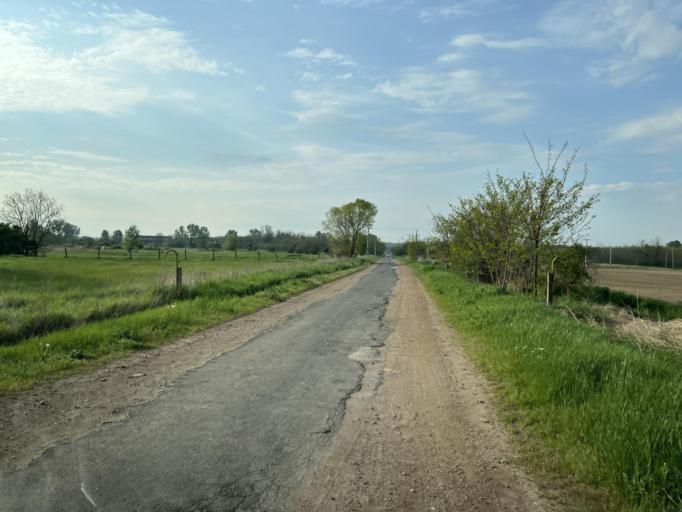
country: HU
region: Pest
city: Albertirsa
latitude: 47.2676
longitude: 19.6055
